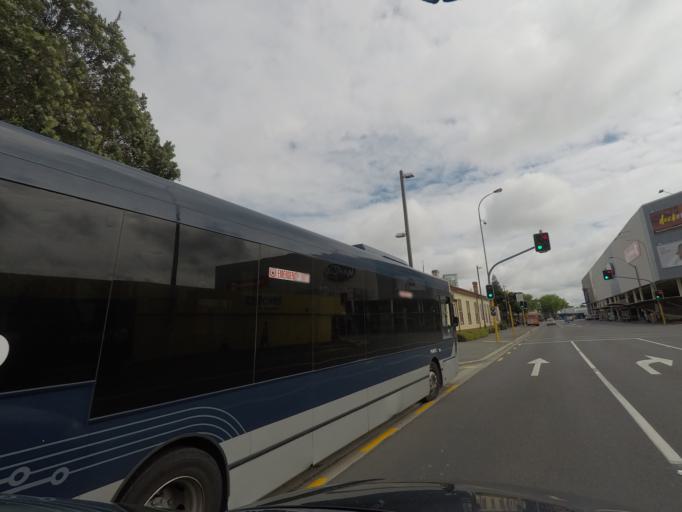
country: NZ
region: Auckland
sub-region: Auckland
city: Rosebank
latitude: -36.8822
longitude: 174.6313
